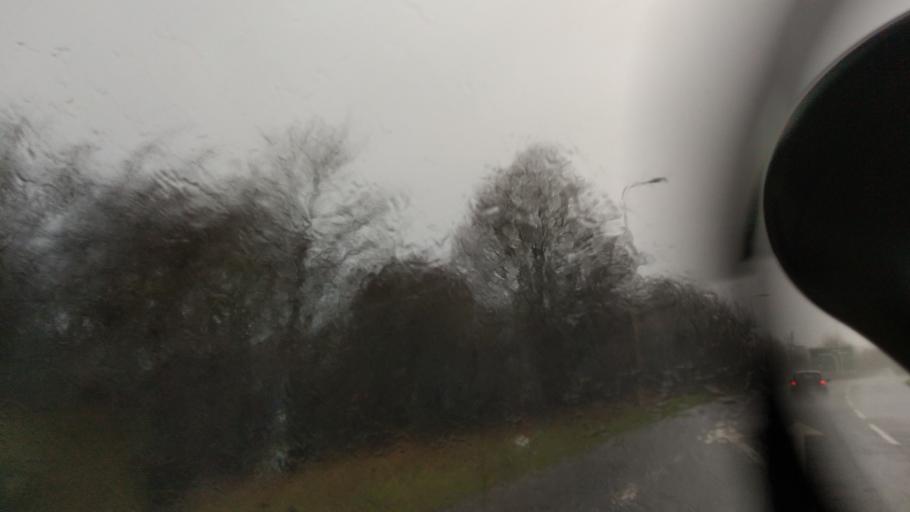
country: GB
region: England
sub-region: West Sussex
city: Fontwell
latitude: 50.8540
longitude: -0.6373
